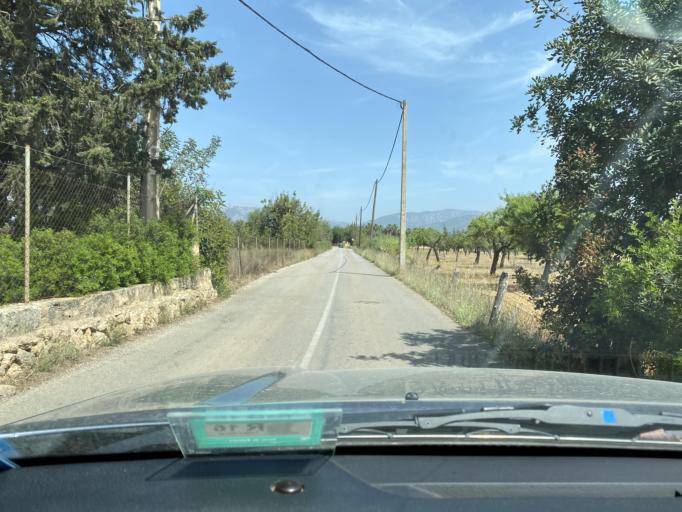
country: ES
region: Balearic Islands
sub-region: Illes Balears
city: Marratxi
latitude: 39.6285
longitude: 2.7110
